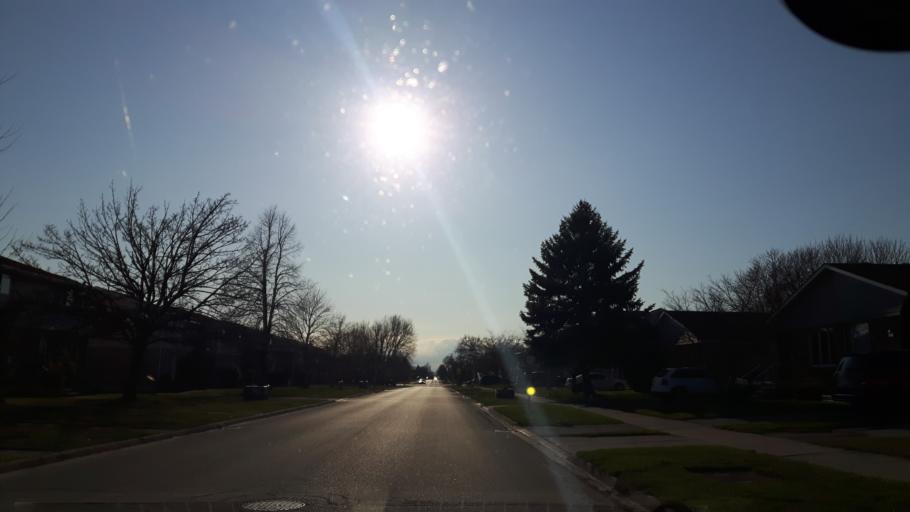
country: CA
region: Ontario
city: Goderich
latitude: 43.7336
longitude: -81.7034
